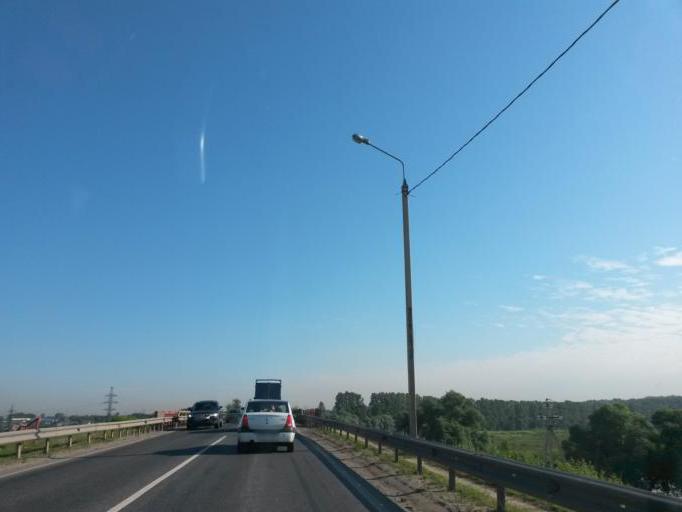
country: RU
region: Moskovskaya
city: Yam
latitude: 55.4919
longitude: 37.7504
